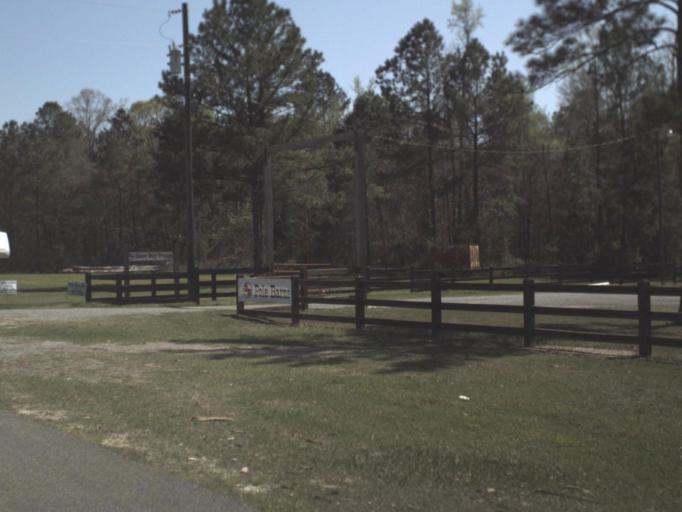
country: US
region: Florida
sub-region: Liberty County
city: Bristol
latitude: 30.3958
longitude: -84.8077
